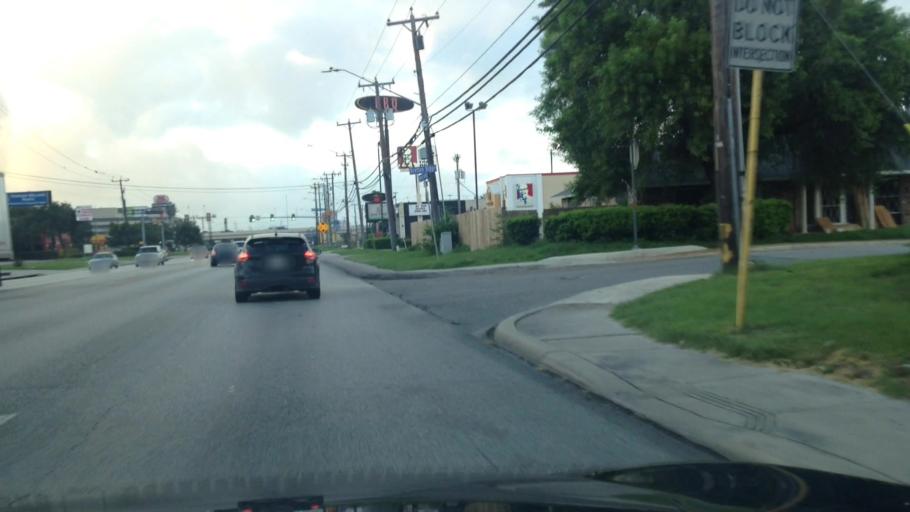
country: US
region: Texas
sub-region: Bexar County
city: Windcrest
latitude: 29.5199
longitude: -98.4111
